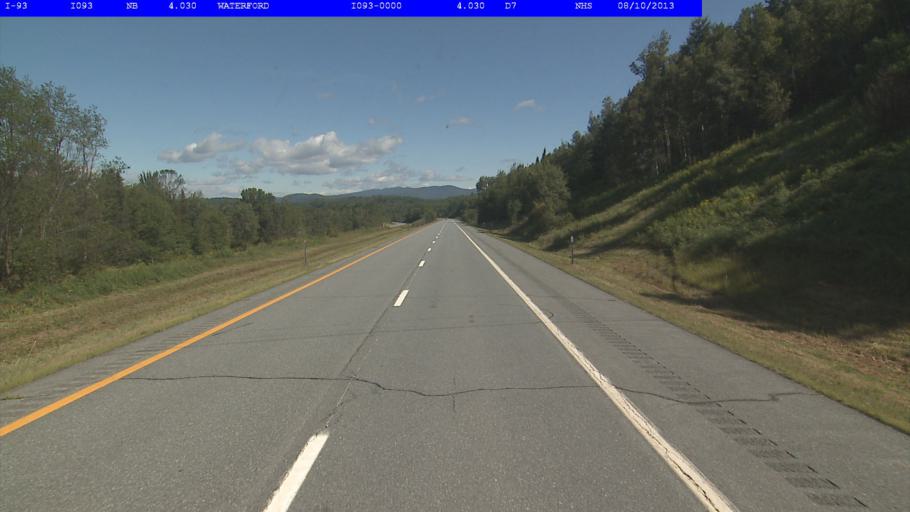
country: US
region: Vermont
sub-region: Caledonia County
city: Saint Johnsbury
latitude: 44.3936
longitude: -71.9207
